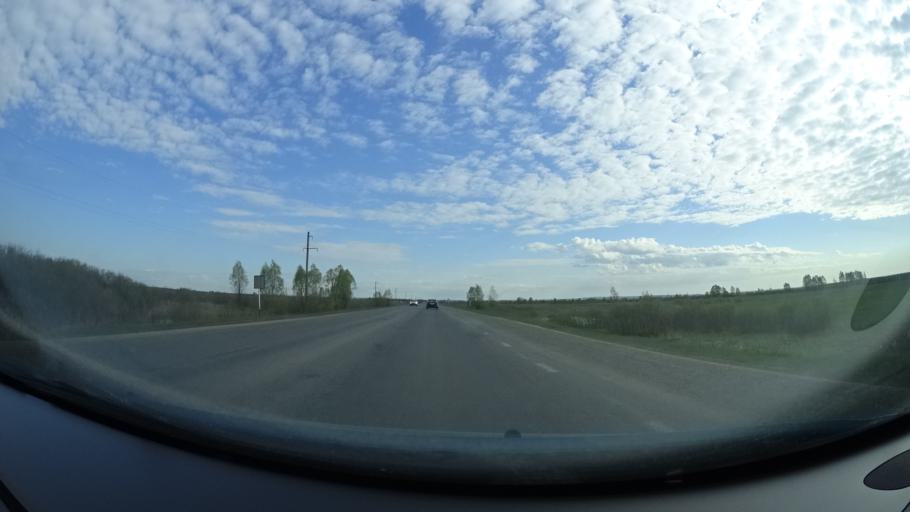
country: RU
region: Bashkortostan
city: Blagoveshchensk
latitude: 54.9821
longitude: 55.7712
